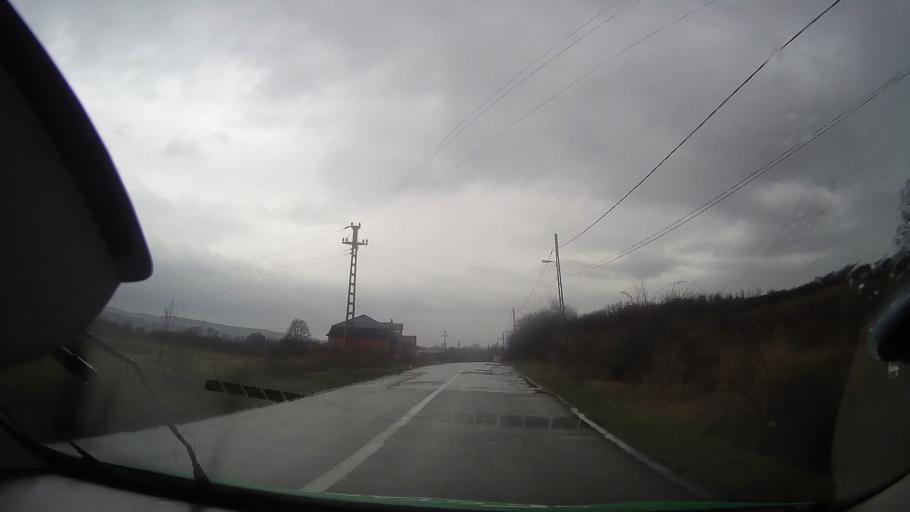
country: RO
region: Bihor
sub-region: Comuna Soimi
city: Soimi
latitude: 46.6830
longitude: 22.1158
